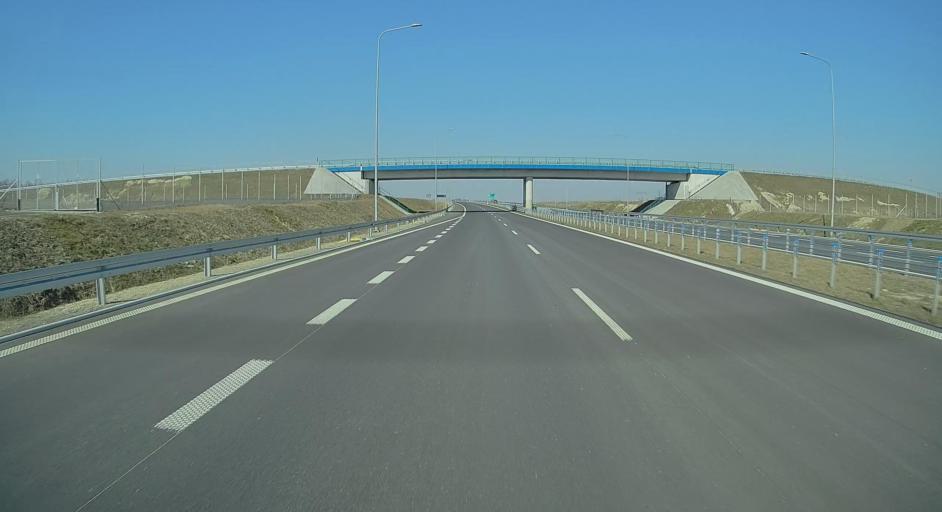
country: PL
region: Lublin Voivodeship
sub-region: Powiat janowski
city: Modliborzyce
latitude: 50.7327
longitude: 22.3486
